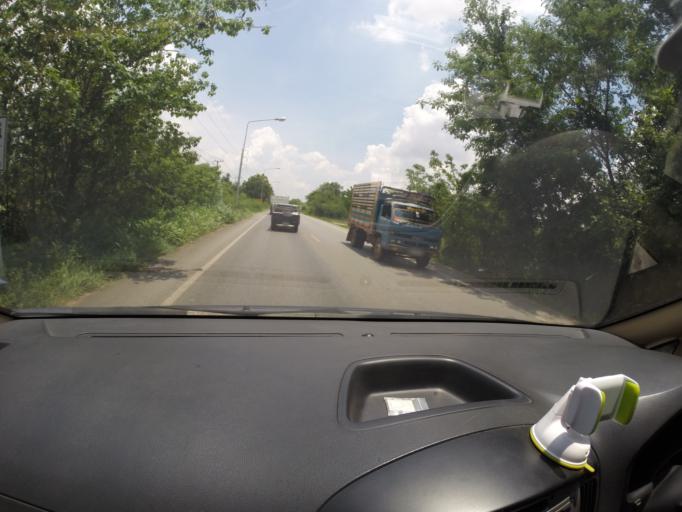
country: TH
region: Nakhon Ratchasima
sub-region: Amphoe Thepharak
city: Thepharak
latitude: 15.1220
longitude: 101.5150
